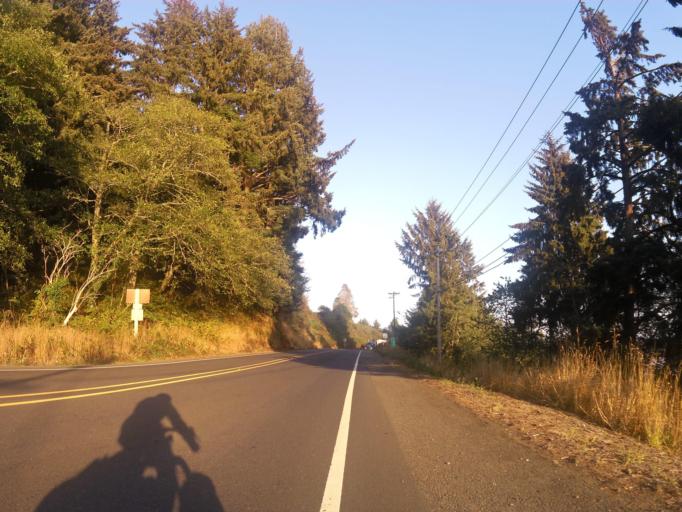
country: US
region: Oregon
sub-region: Tillamook County
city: Bay City
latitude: 45.5589
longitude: -123.9262
